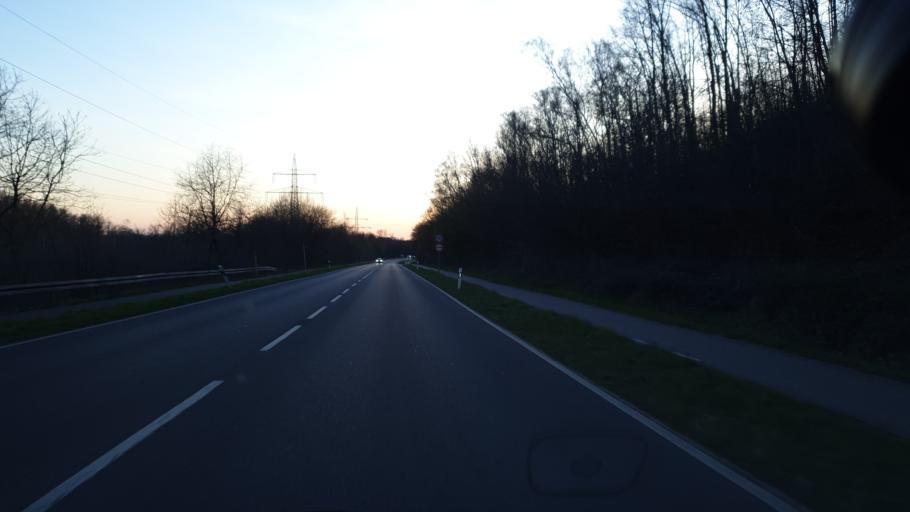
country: DE
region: North Rhine-Westphalia
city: Tuernich
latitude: 50.9256
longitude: 6.7389
